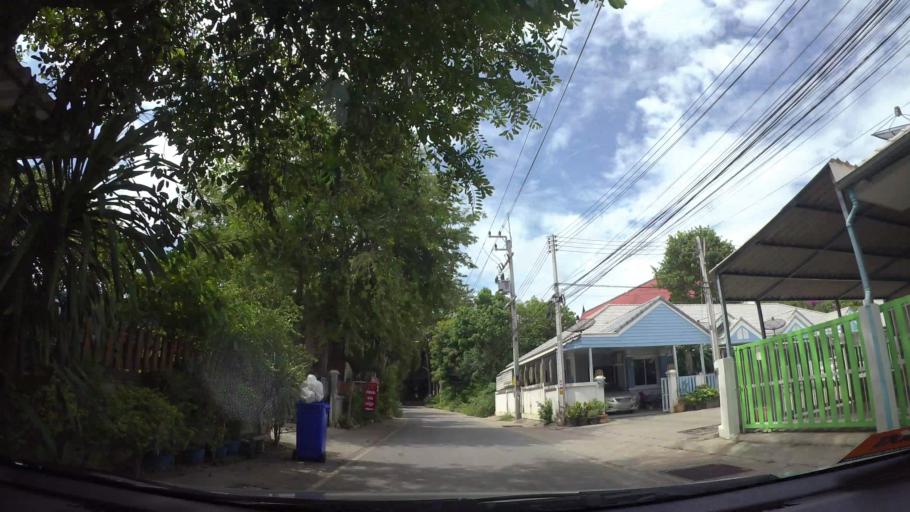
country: TH
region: Chon Buri
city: Sattahip
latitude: 12.6808
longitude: 100.9071
